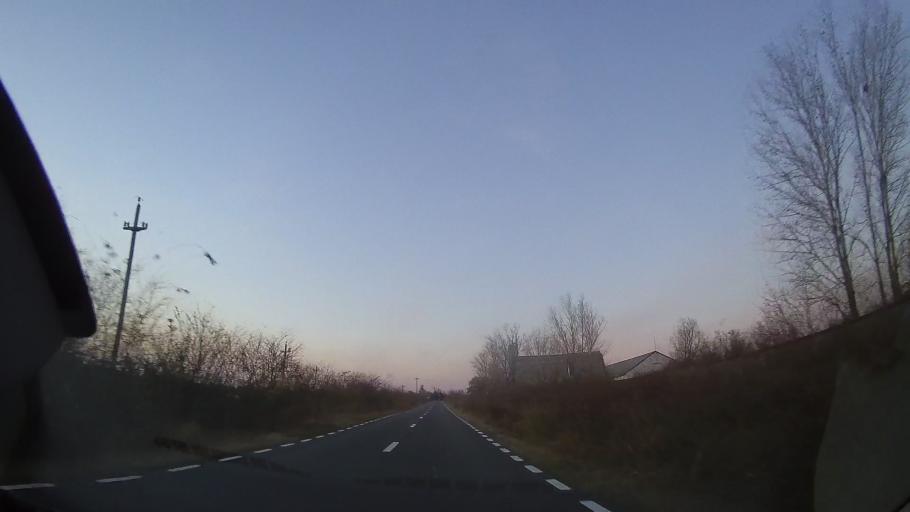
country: RO
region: Constanta
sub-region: Comuna Cobadin
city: Cobadin
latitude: 44.0493
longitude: 28.2499
